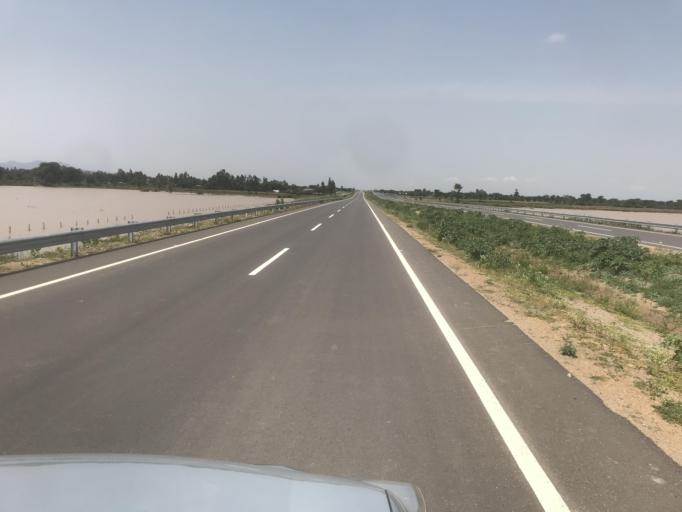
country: ET
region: Oromiya
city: Mojo
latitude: 8.3834
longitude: 39.0053
